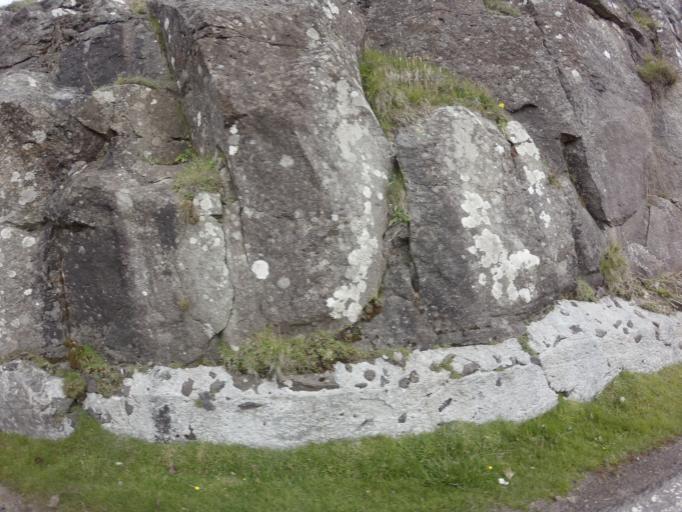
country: FO
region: Sandoy
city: Sandur
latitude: 61.8334
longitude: -6.7829
